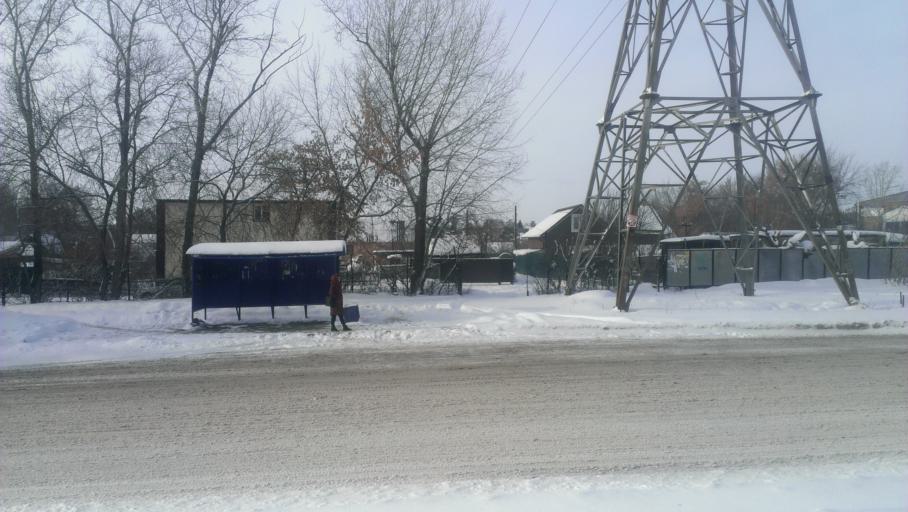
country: RU
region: Altai Krai
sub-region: Gorod Barnaulskiy
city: Barnaul
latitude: 53.3867
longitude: 83.6840
